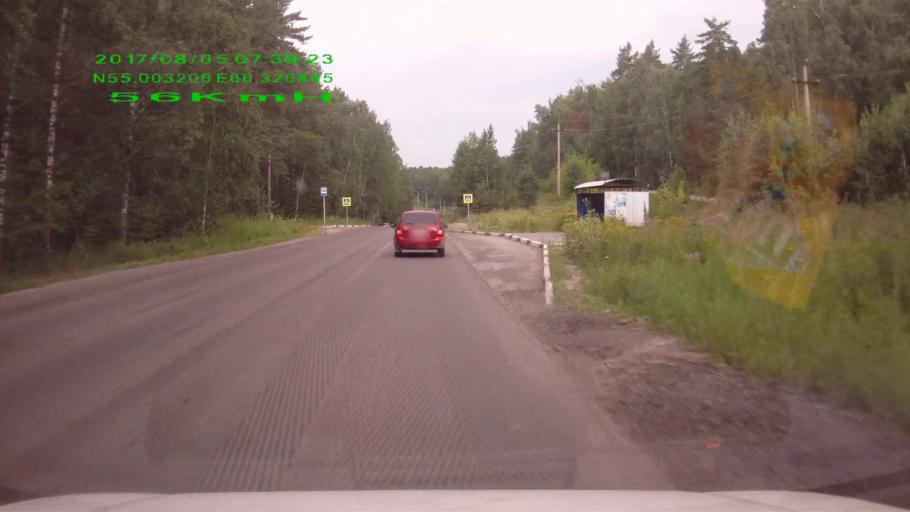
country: RU
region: Chelyabinsk
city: Chebarkul'
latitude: 55.0033
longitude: 60.3266
